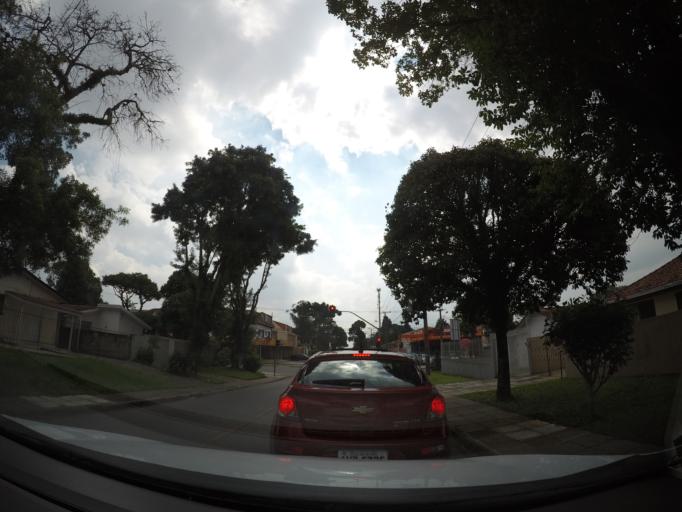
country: BR
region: Parana
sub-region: Sao Jose Dos Pinhais
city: Sao Jose dos Pinhais
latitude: -25.5002
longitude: -49.2507
